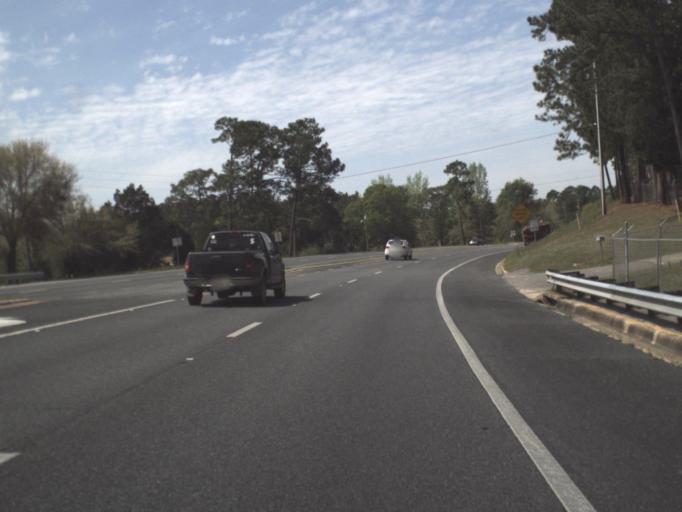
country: US
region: Florida
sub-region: Okaloosa County
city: Crestview
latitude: 30.7541
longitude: -86.6163
